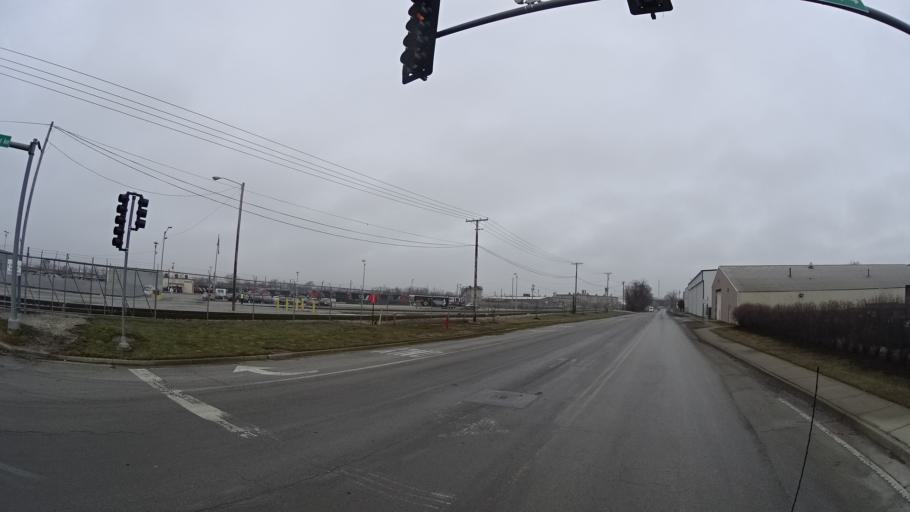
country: US
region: Illinois
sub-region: Cook County
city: East Hazel Crest
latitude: 41.5719
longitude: -87.6556
